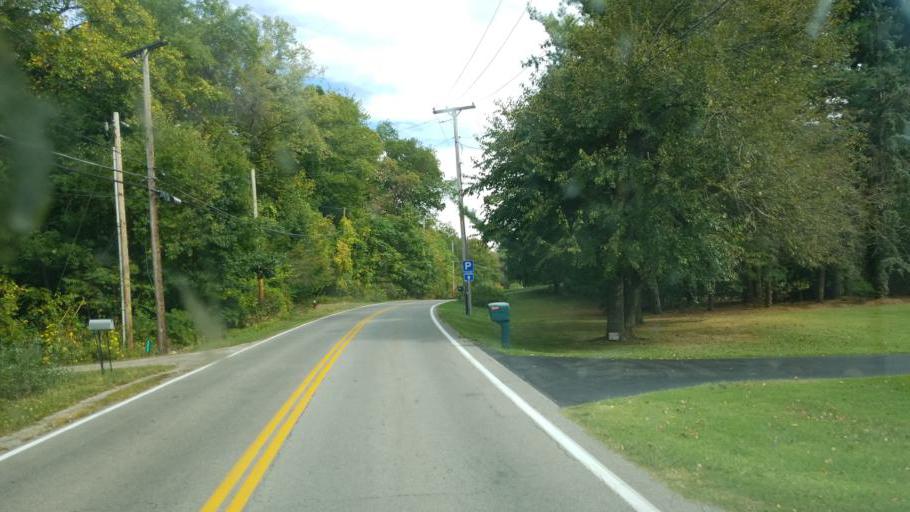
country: US
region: Ohio
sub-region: Lorain County
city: Amherst
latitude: 41.3984
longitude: -82.2526
